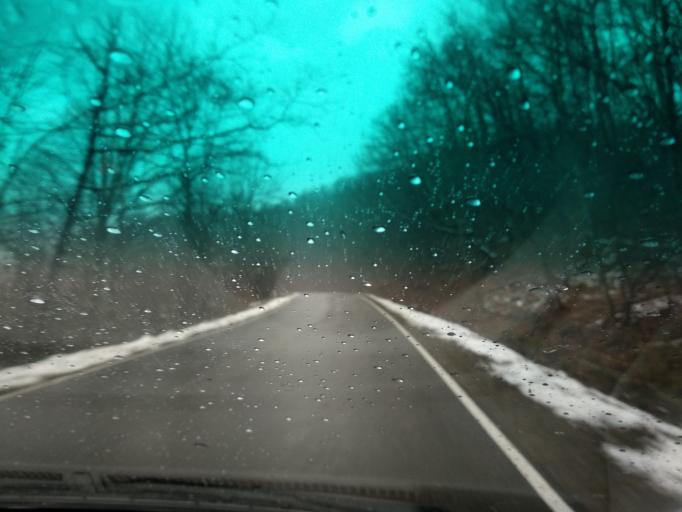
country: RU
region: Krasnodarskiy
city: Khadyzhensk
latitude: 44.2645
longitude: 39.3634
